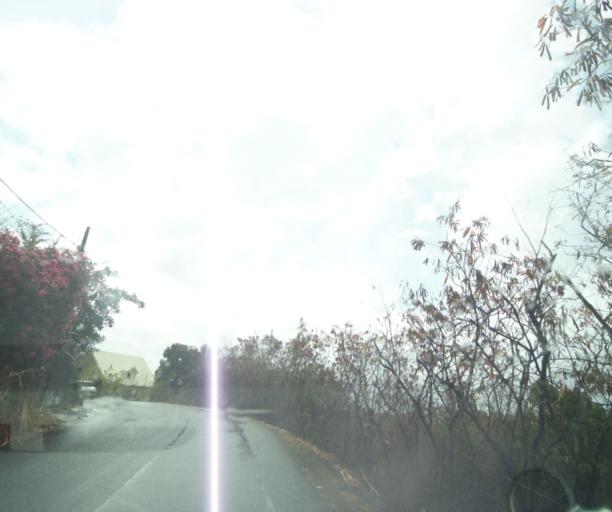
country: RE
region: Reunion
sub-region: Reunion
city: La Possession
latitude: -20.9766
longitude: 55.3297
